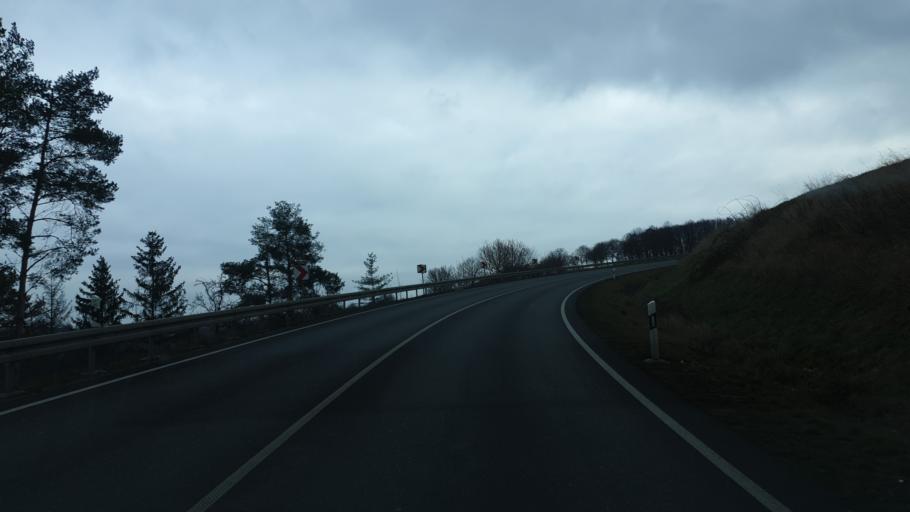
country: DE
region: Saxony-Anhalt
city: Wethau
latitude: 51.1342
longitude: 11.8695
